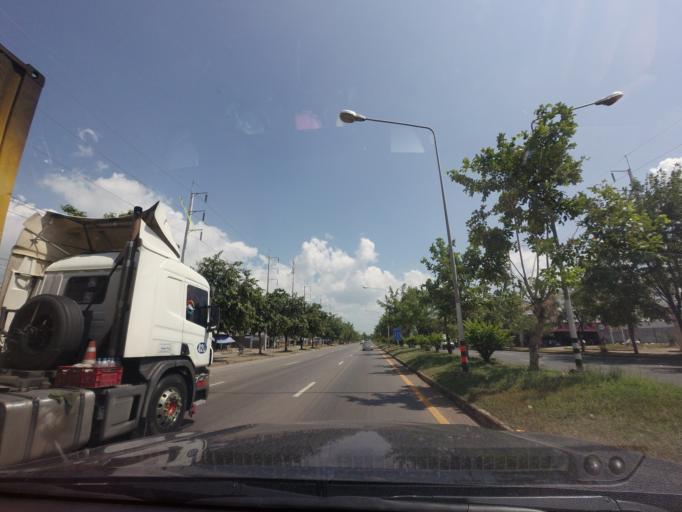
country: TH
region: Phetchabun
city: Nong Phai
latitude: 16.0799
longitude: 101.0599
